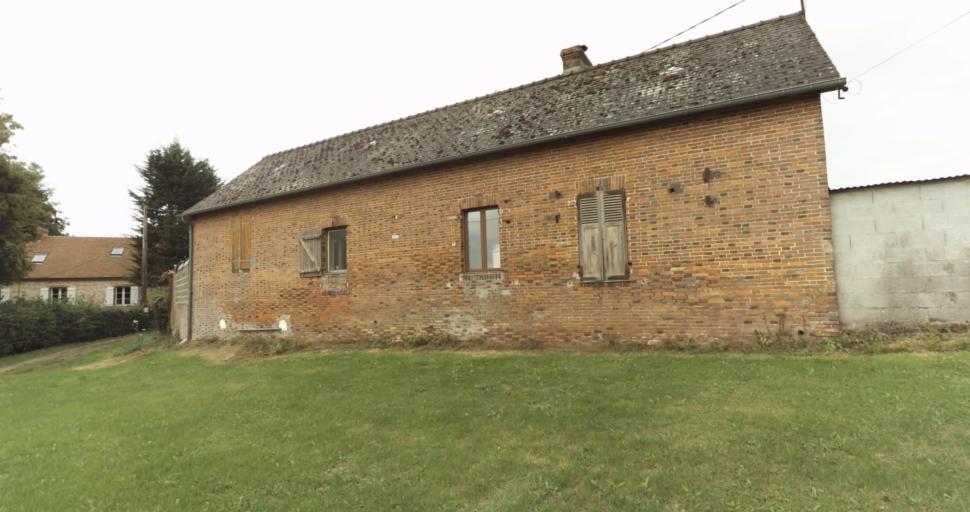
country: FR
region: Lower Normandy
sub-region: Departement de l'Orne
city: Gace
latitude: 48.7253
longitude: 0.3249
